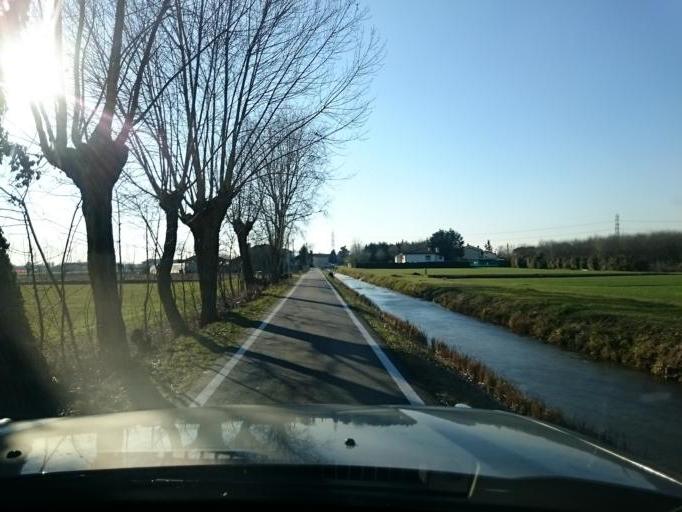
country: IT
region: Veneto
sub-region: Provincia di Venezia
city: Mira Taglio
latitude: 45.4269
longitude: 12.1154
